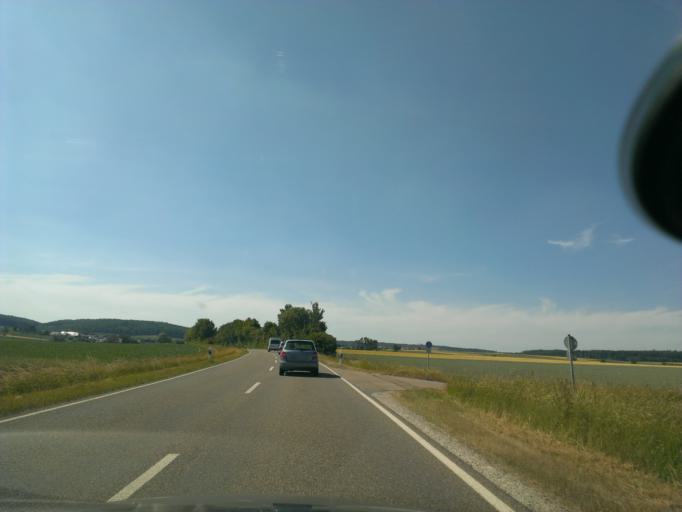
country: DE
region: Bavaria
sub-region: Swabia
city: Tapfheim
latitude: 48.6902
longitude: 10.6878
